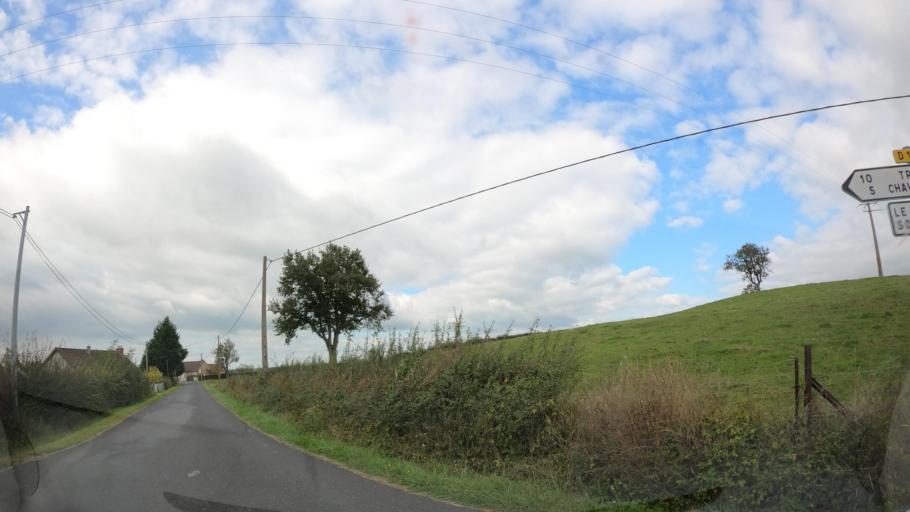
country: FR
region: Auvergne
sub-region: Departement de l'Allier
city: Lapalisse
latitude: 46.3426
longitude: 3.6406
